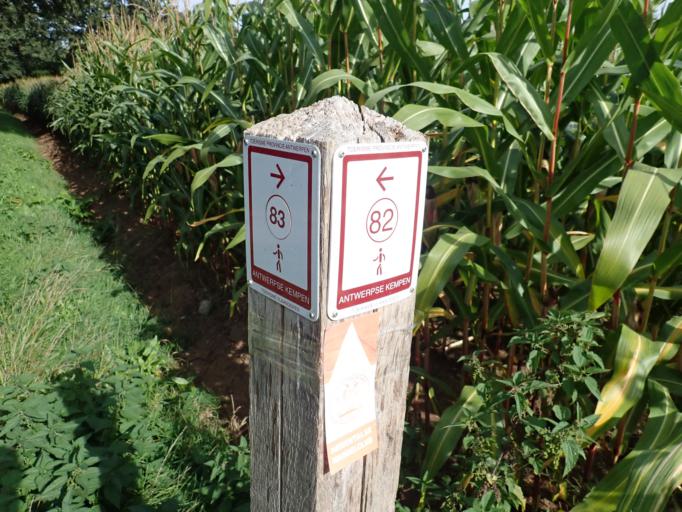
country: BE
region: Flanders
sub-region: Provincie Antwerpen
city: Lille
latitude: 51.2266
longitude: 4.8262
